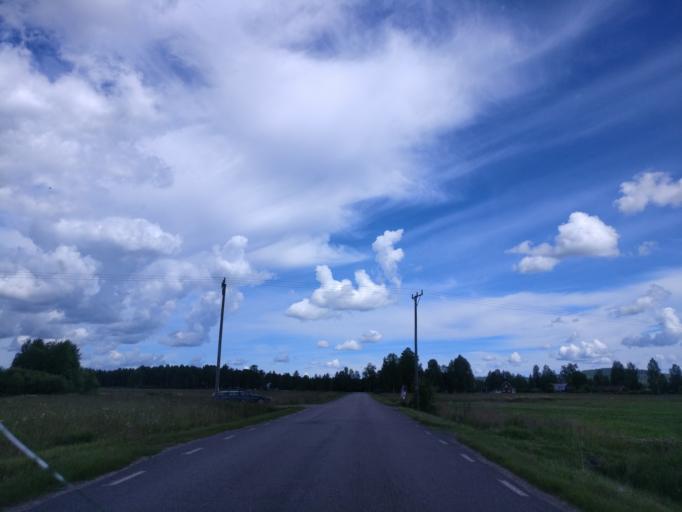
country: SE
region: Vaermland
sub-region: Hagfors Kommun
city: Ekshaerad
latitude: 60.1266
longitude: 13.4561
